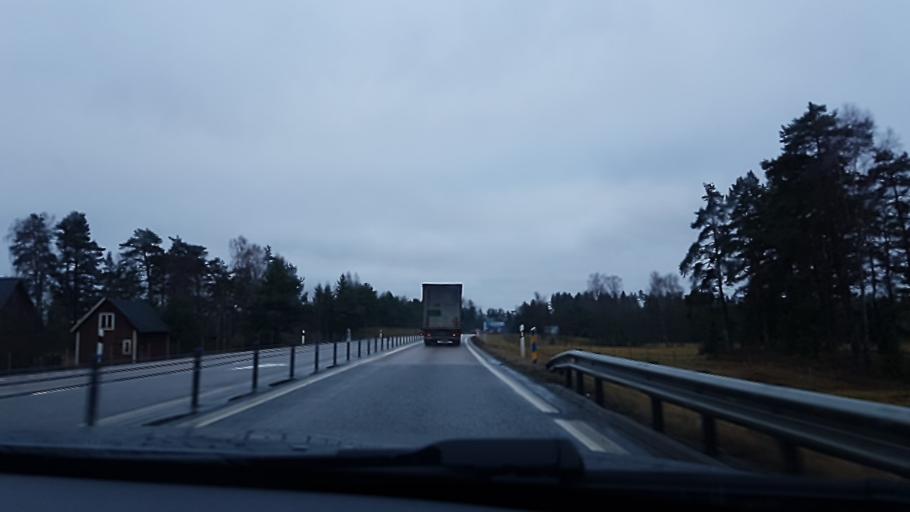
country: SE
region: Kronoberg
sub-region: Ljungby Kommun
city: Lagan
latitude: 56.9465
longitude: 13.9998
